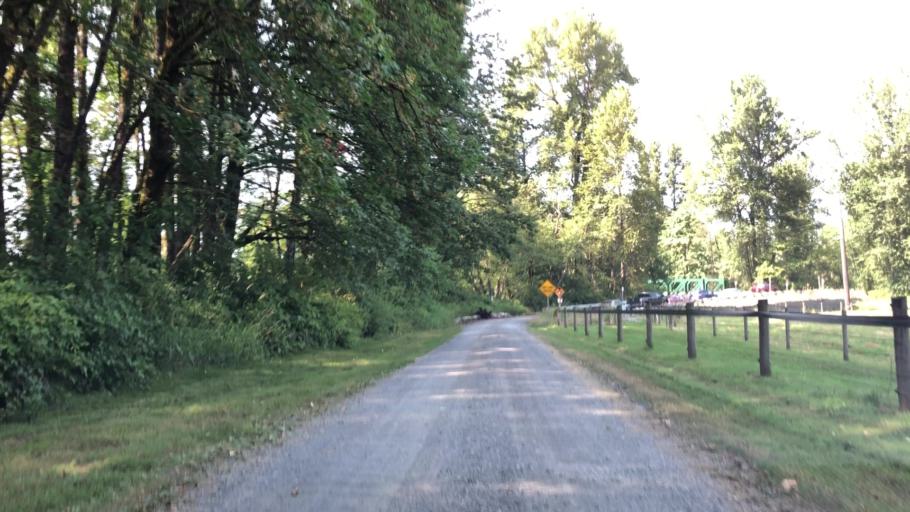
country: US
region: Washington
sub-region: Snohomish County
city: Lochsloy
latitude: 48.0515
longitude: -122.0237
